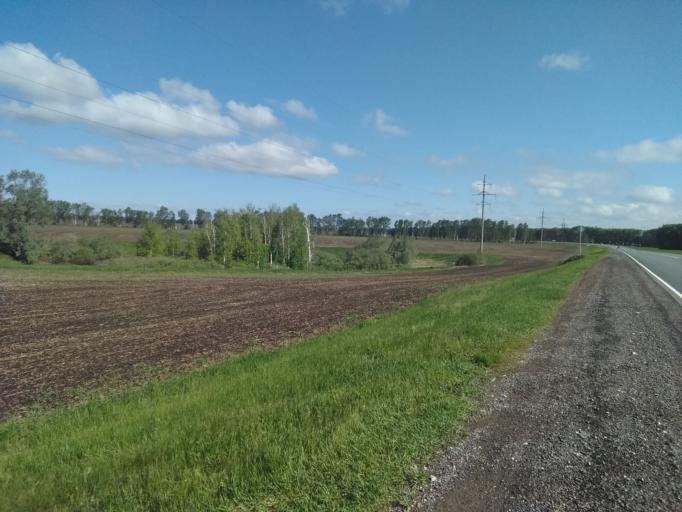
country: RU
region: Bashkortostan
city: Kushnarenkovo
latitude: 55.1751
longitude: 55.1272
